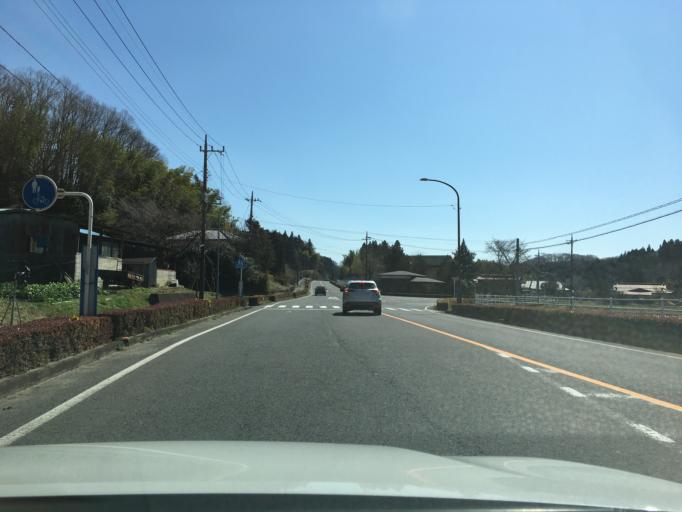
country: JP
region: Tochigi
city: Kuroiso
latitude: 37.0416
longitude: 140.1706
